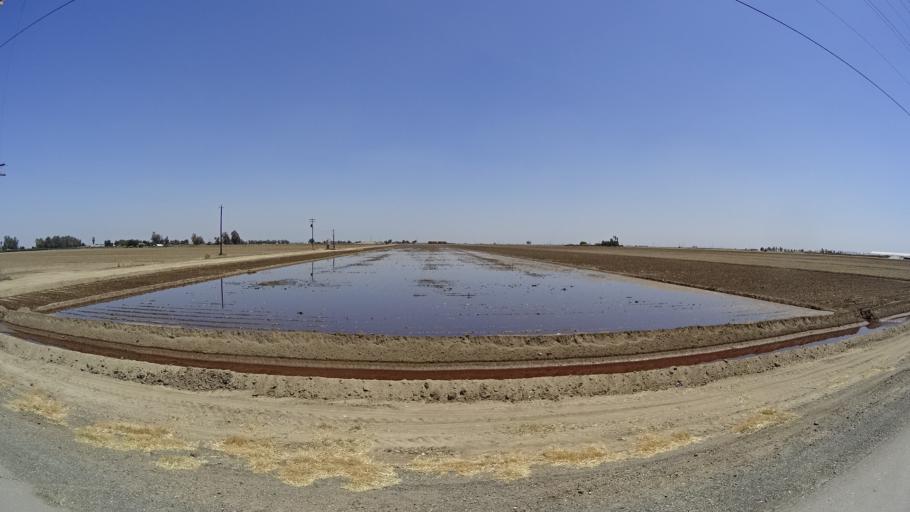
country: US
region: California
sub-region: Kings County
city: Home Garden
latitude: 36.2071
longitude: -119.6457
